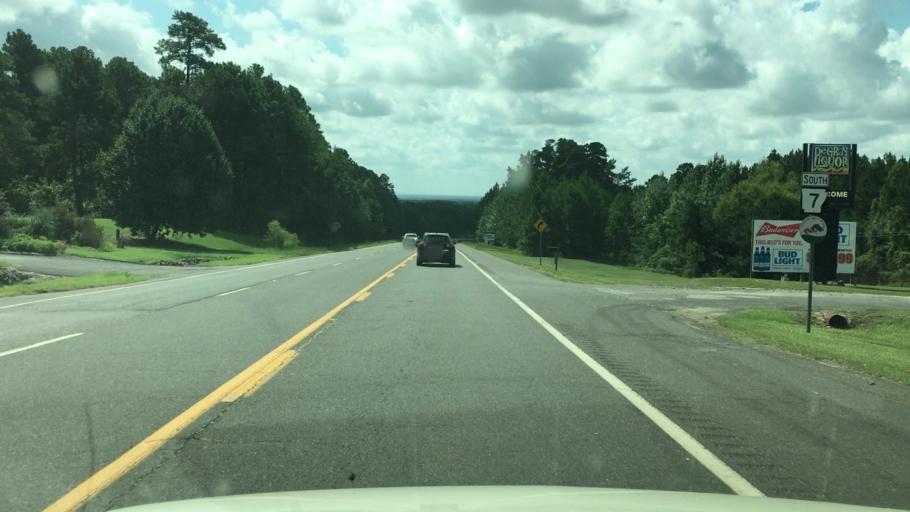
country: US
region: Arkansas
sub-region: Clark County
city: Arkadelphia
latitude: 34.2143
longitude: -93.0835
